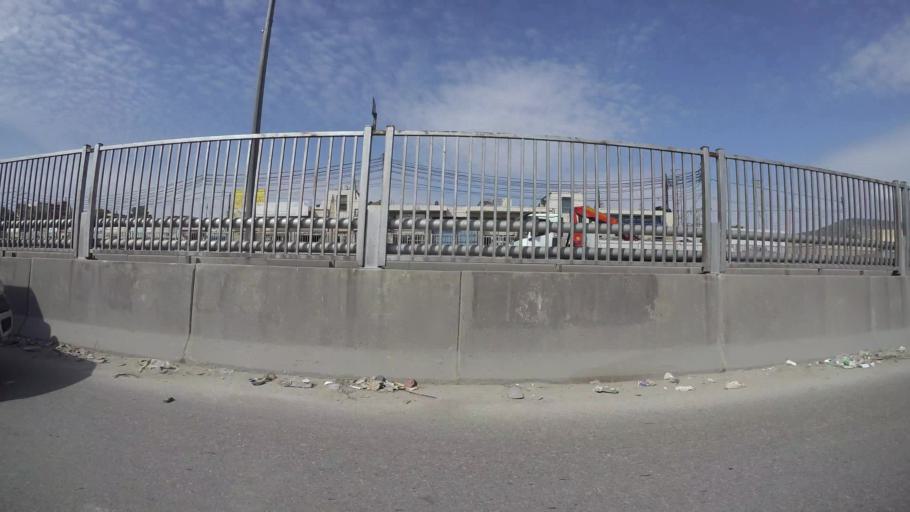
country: JO
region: Amman
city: Al Jubayhah
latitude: 32.0788
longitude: 35.8391
